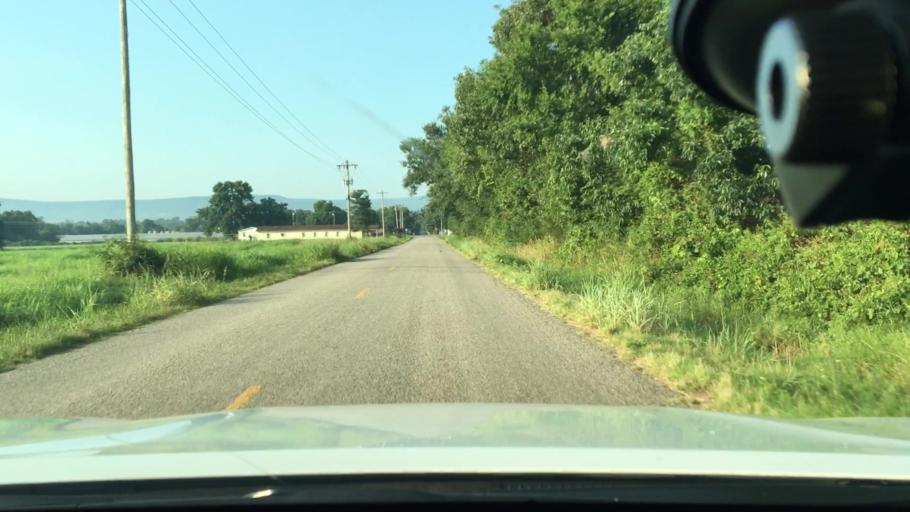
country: US
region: Arkansas
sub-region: Johnson County
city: Coal Hill
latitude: 35.3399
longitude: -93.6138
